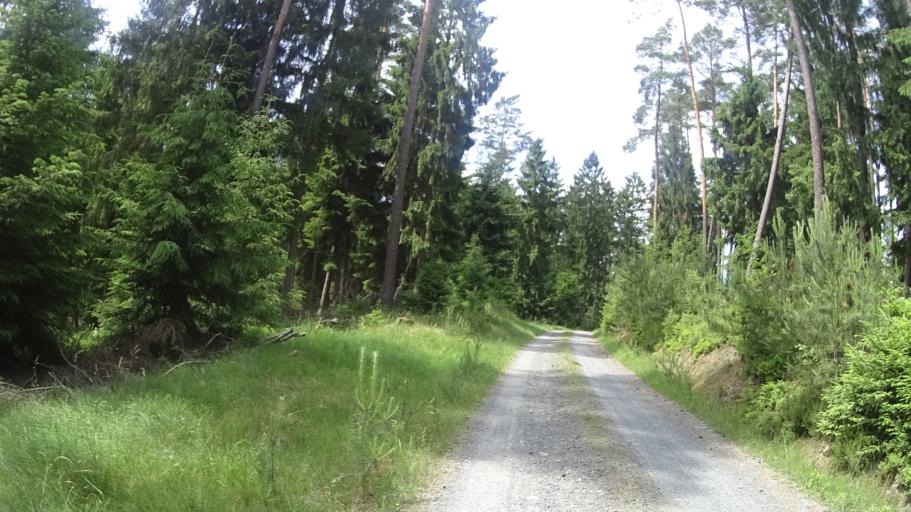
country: DE
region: Hesse
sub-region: Regierungsbezirk Giessen
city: Munchhausen
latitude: 50.9509
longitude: 8.7919
